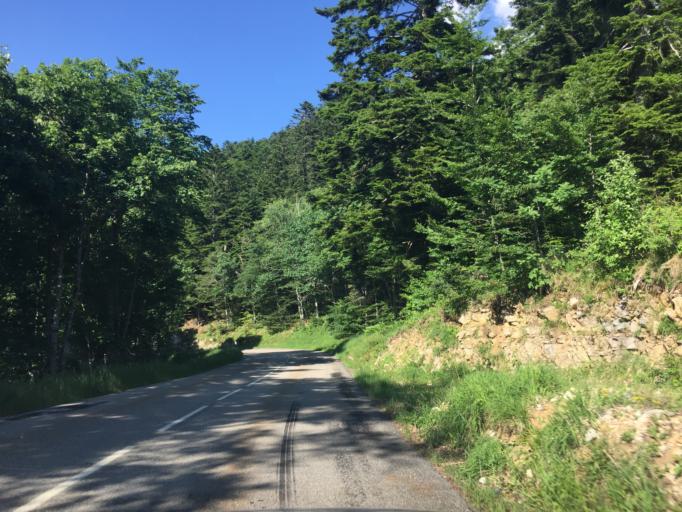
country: FR
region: Rhone-Alpes
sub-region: Departement de la Drome
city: Saint-Jean-en-Royans
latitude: 44.9308
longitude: 5.3226
